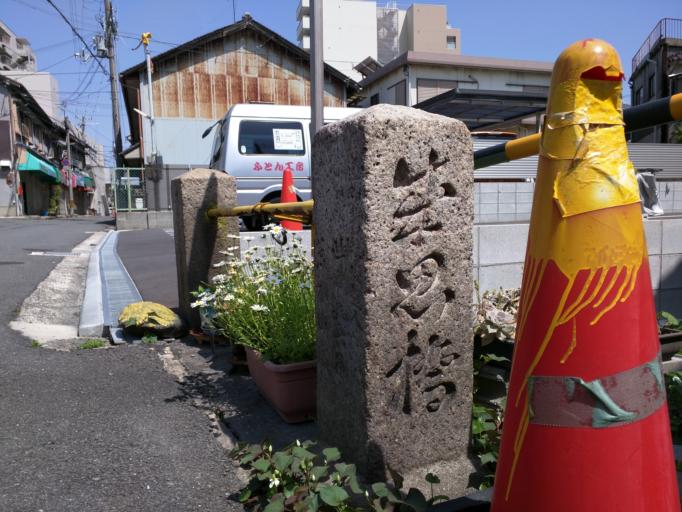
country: JP
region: Osaka
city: Yao
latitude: 34.6285
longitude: 135.5958
